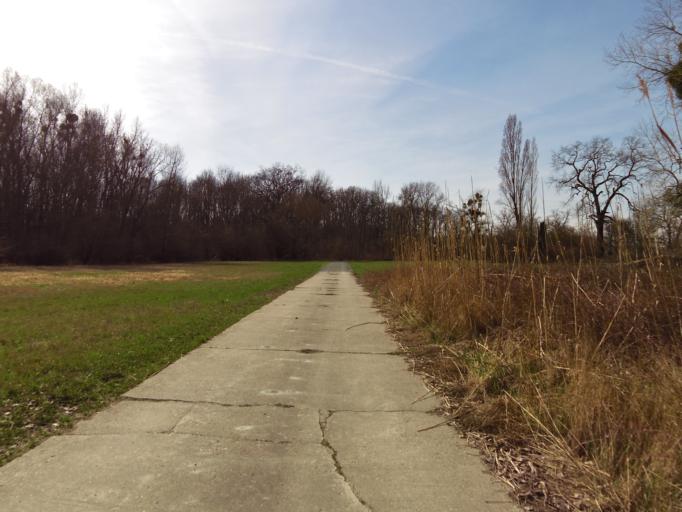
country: DE
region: Rheinland-Pfalz
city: Gimbsheim
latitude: 49.8065
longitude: 8.4159
